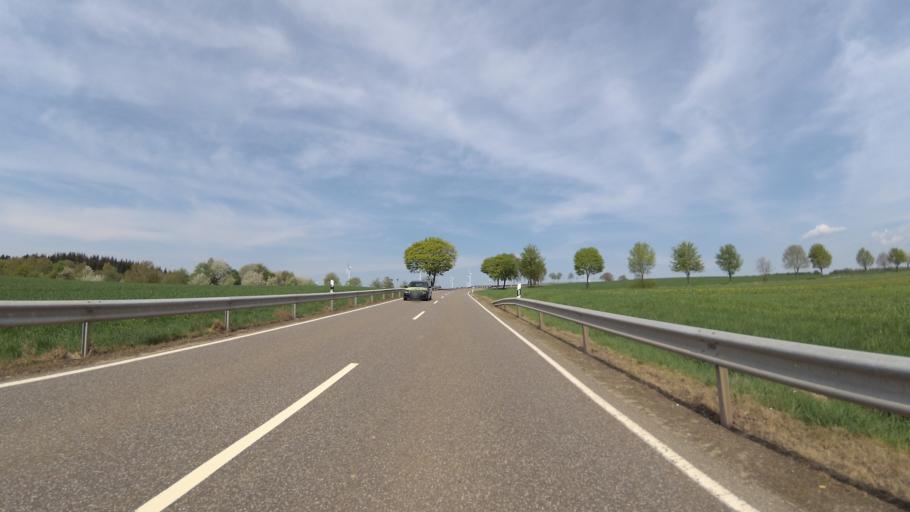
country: DE
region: Rheinland-Pfalz
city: Morbach
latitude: 49.8209
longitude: 7.1268
